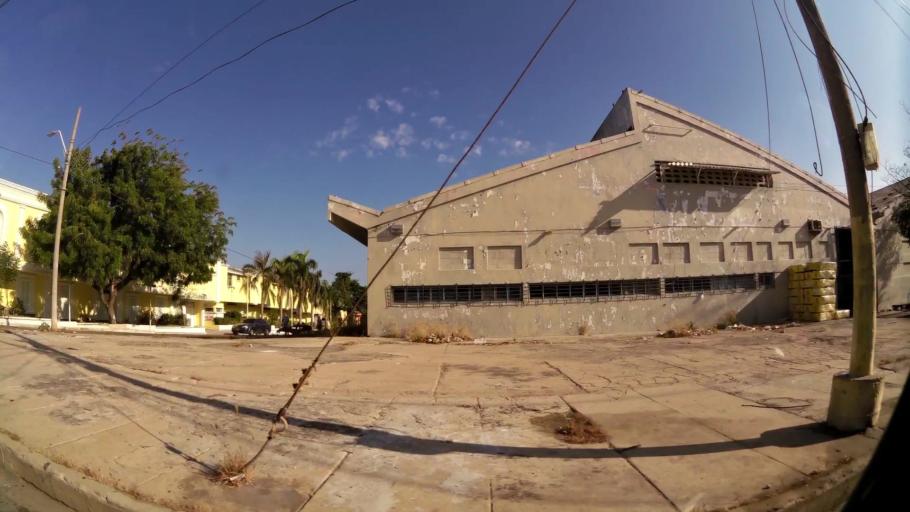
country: CO
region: Atlantico
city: Barranquilla
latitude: 10.9899
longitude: -74.7824
